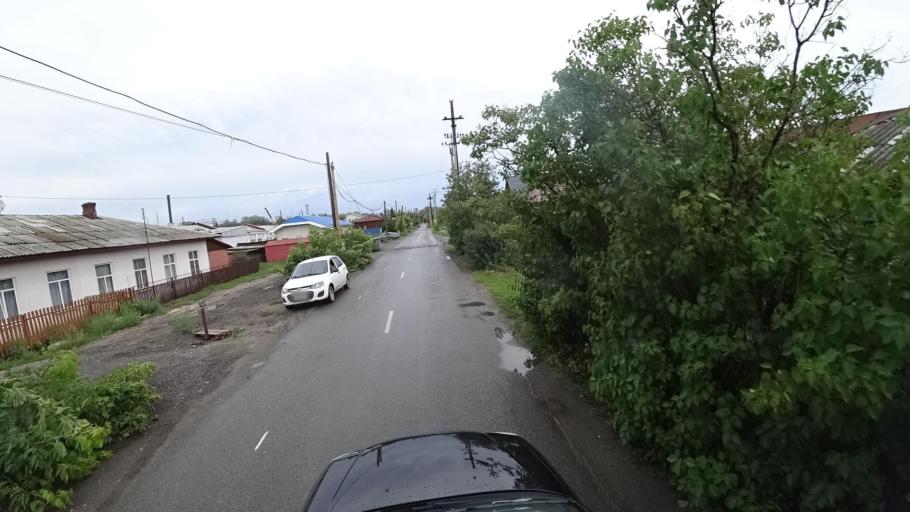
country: RU
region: Sverdlovsk
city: Kamyshlov
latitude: 56.8476
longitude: 62.7148
